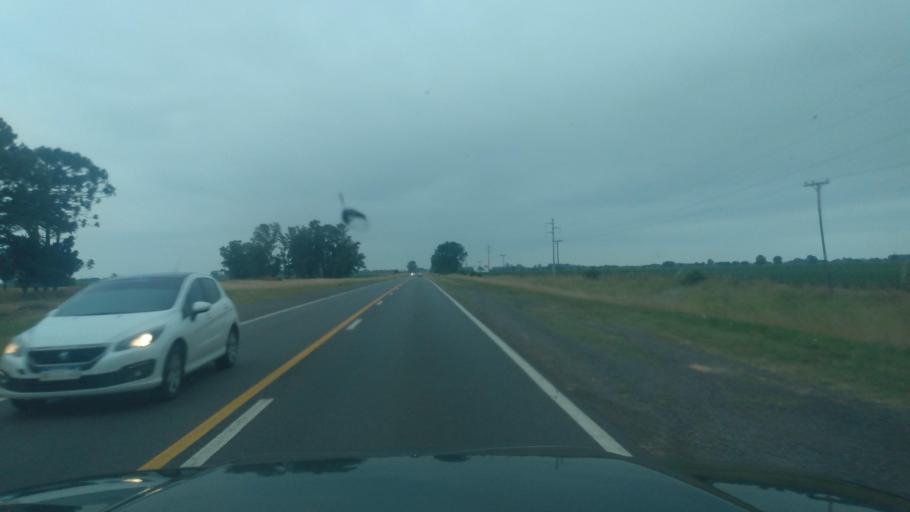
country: AR
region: Buenos Aires
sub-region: Partido de Chivilcoy
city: Chivilcoy
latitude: -34.9924
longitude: -60.0912
